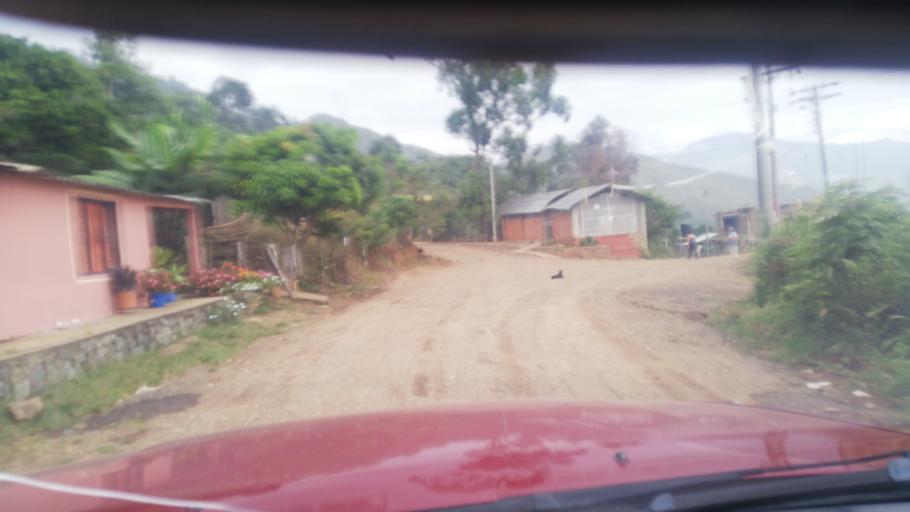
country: CO
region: Valle del Cauca
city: Cali
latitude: 3.5092
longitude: -76.5423
